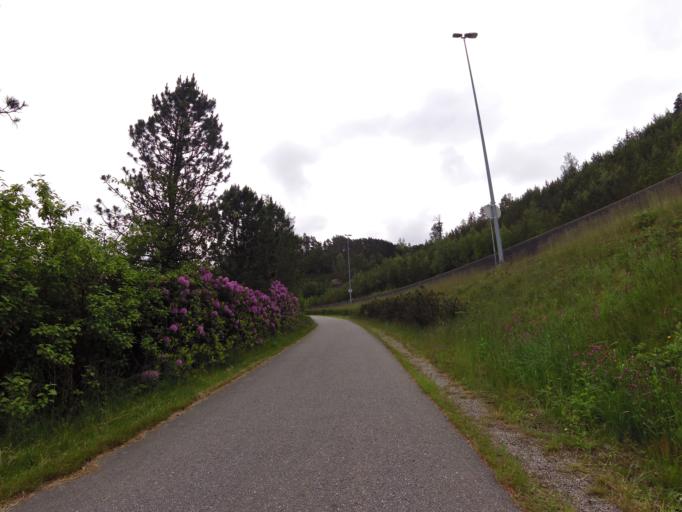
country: NO
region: Vest-Agder
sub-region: Flekkefjord
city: Flekkefjord
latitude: 58.2967
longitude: 6.6806
